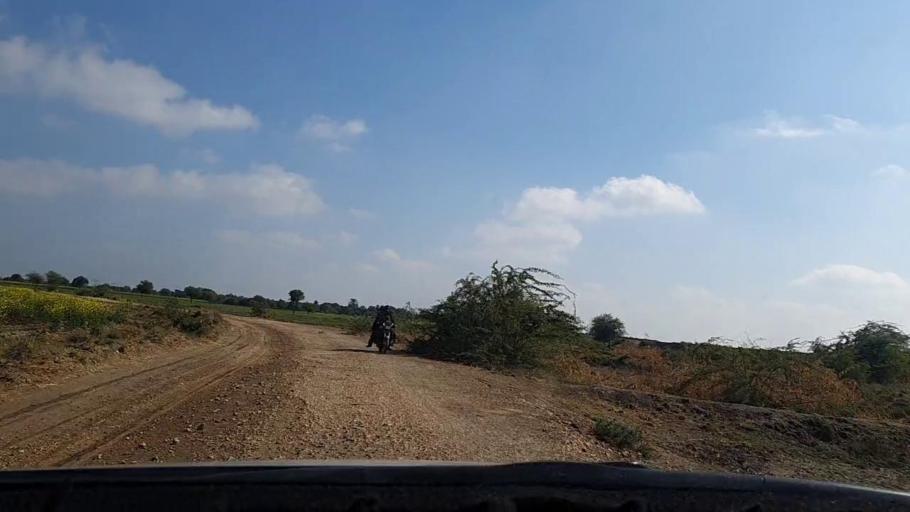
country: PK
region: Sindh
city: Tando Mittha Khan
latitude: 25.7374
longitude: 69.2449
